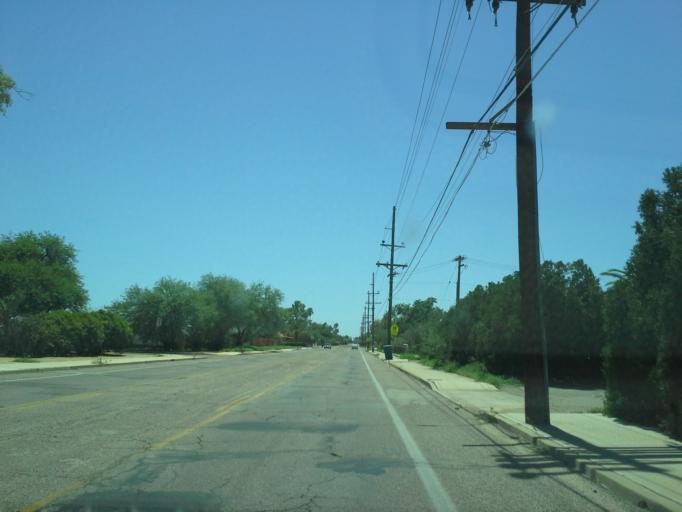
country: US
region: Arizona
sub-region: Pima County
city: Catalina Foothills
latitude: 32.2625
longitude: -110.9353
